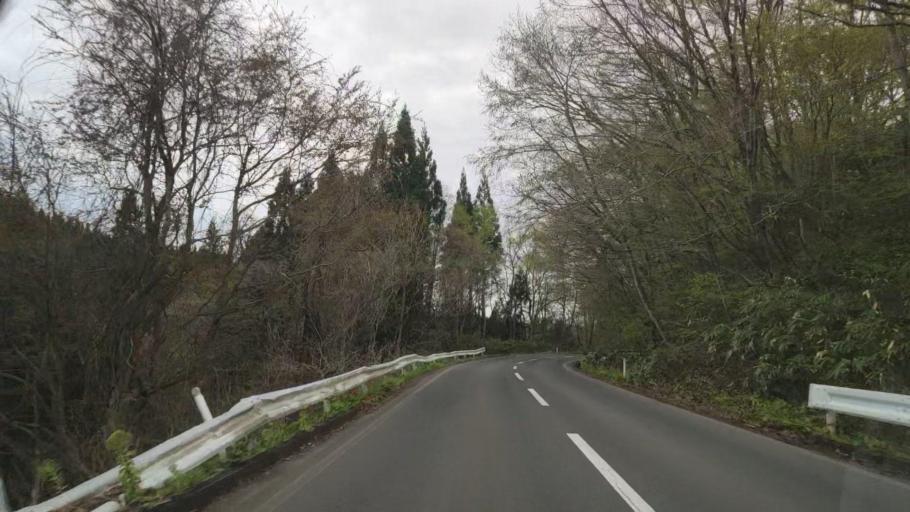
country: JP
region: Akita
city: Hanawa
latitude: 40.3801
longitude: 140.7911
